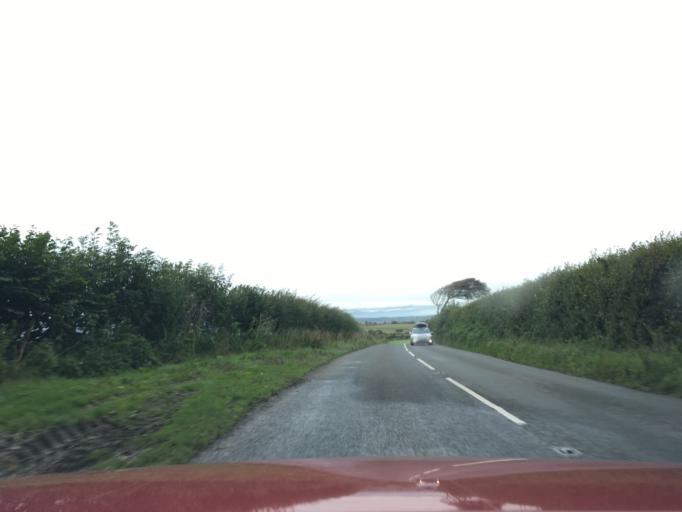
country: GB
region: England
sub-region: Devon
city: Kingsbridge
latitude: 50.2876
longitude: -3.8140
